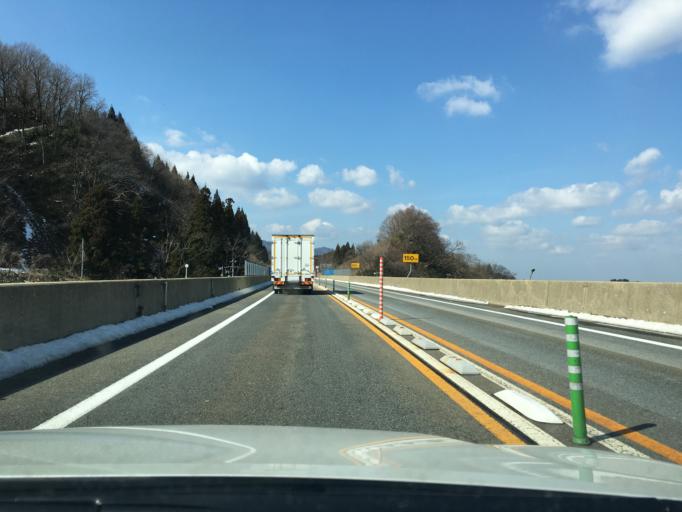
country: JP
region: Yamagata
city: Tsuruoka
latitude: 38.6227
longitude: 139.8423
